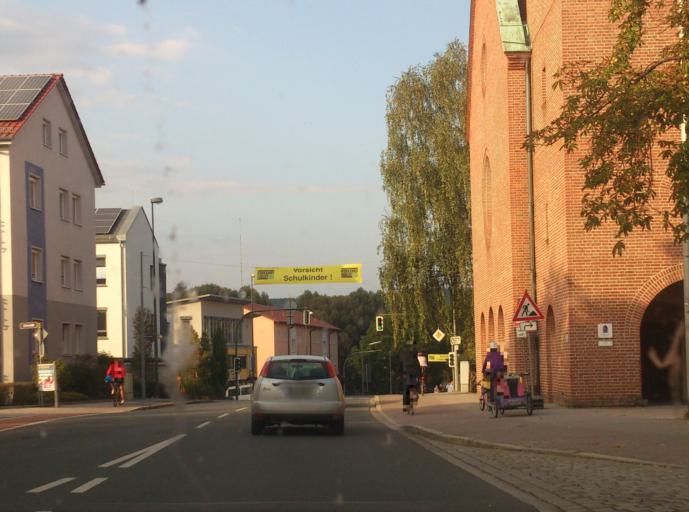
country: DE
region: Bavaria
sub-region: Regierungsbezirk Mittelfranken
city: Buckenhof
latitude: 49.5961
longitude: 11.0362
